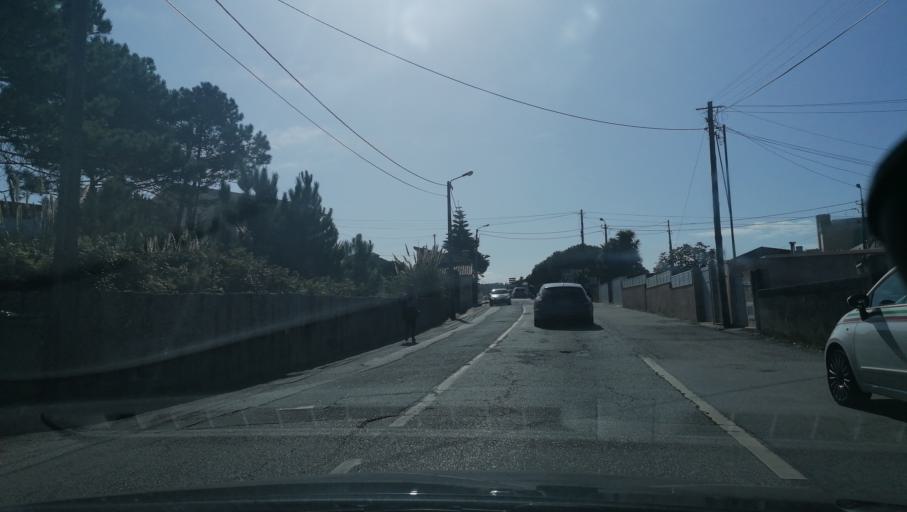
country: PT
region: Porto
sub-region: Vila Nova de Gaia
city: Sao Felix da Marinha
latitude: 41.0316
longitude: -8.6430
